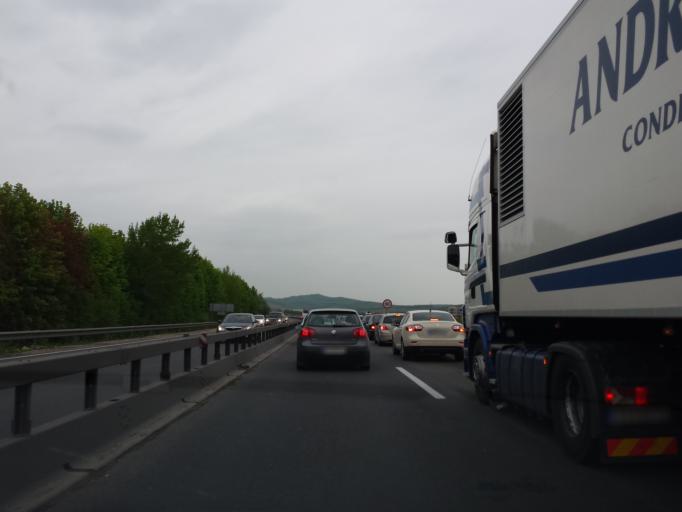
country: HU
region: Pest
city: Toeroekbalint
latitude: 47.4504
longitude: 18.8871
